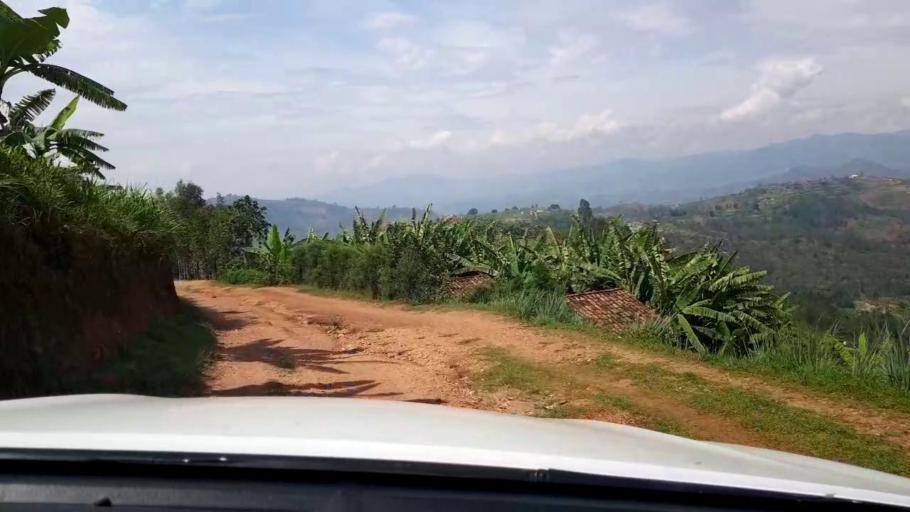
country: RW
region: Southern Province
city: Gitarama
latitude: -2.0556
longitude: 29.6704
